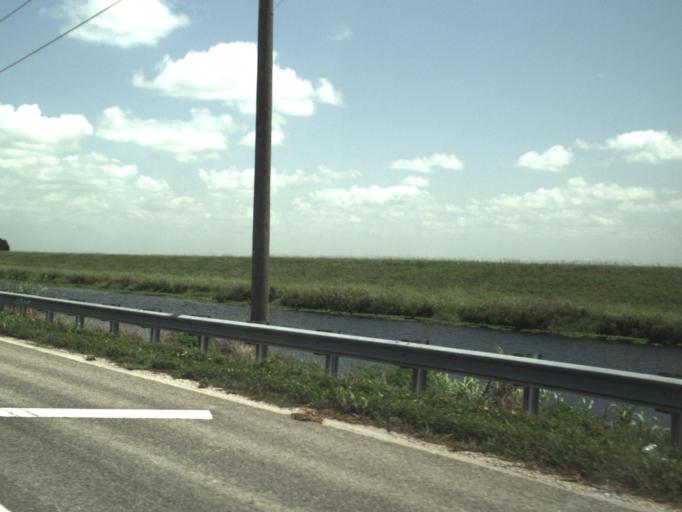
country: US
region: Florida
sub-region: Palm Beach County
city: Belle Glade Camp
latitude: 26.5892
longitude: -80.7109
